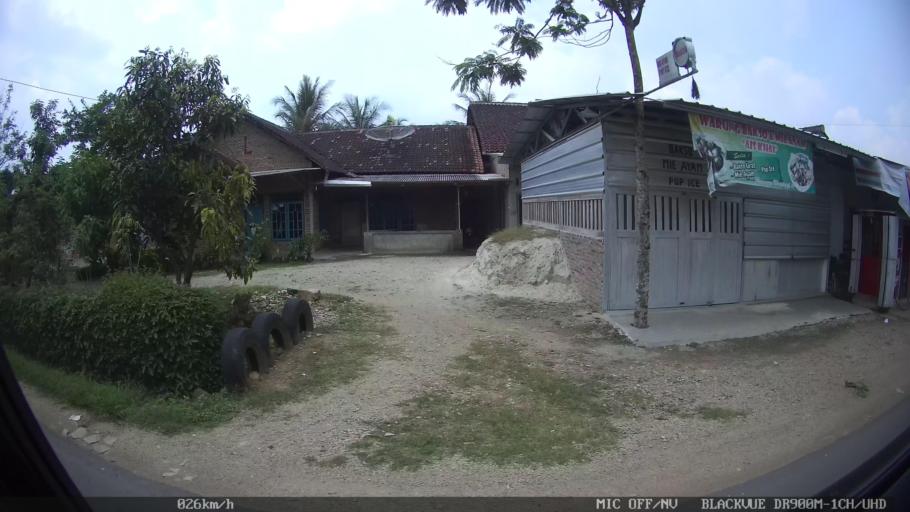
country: ID
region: Lampung
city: Gadingrejo
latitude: -5.3868
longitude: 105.0432
